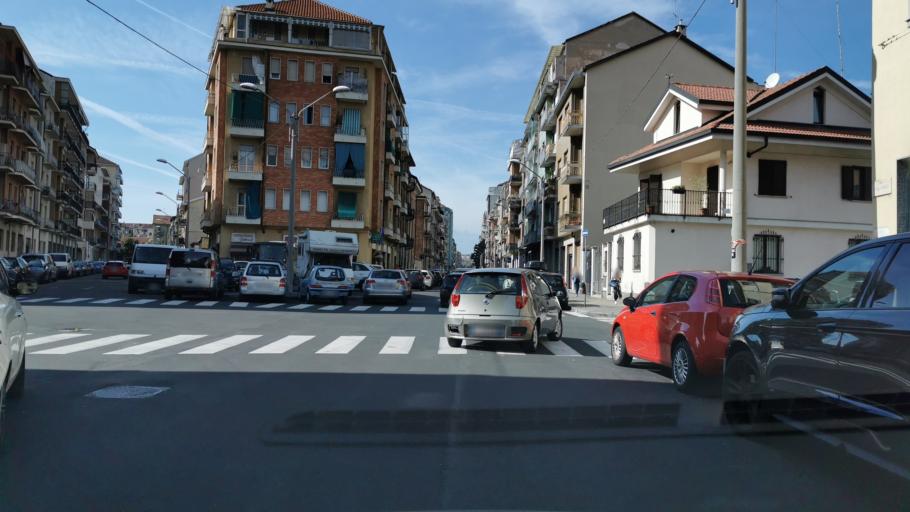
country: IT
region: Piedmont
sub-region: Provincia di Torino
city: Turin
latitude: 45.0984
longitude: 7.6662
